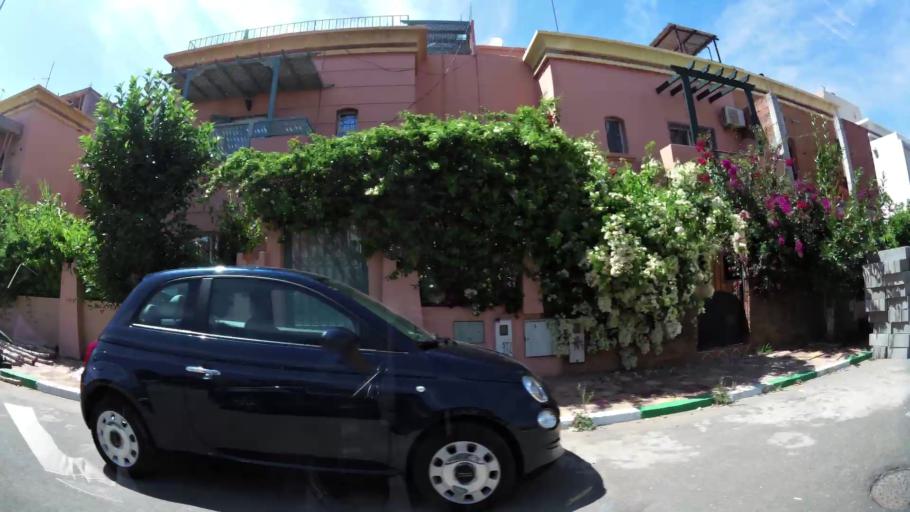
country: MA
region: Marrakech-Tensift-Al Haouz
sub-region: Marrakech
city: Marrakesh
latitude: 31.6502
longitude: -8.0624
